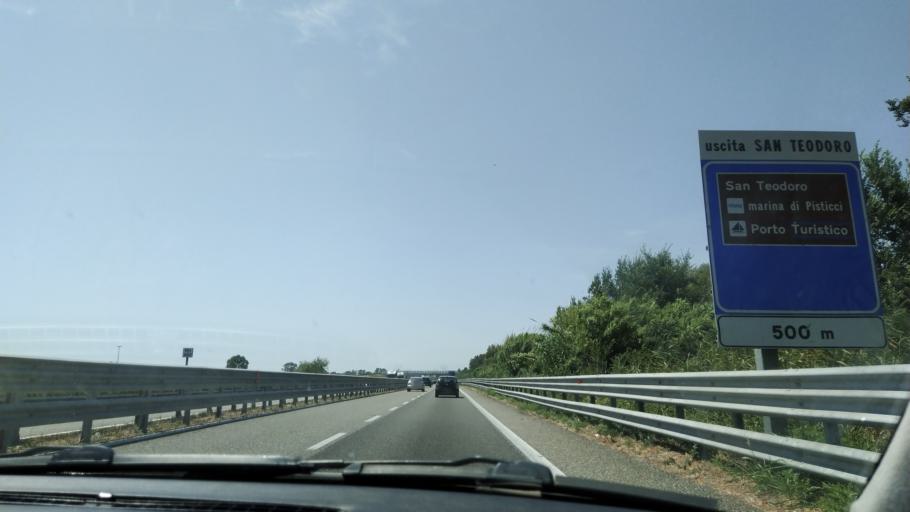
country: IT
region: Basilicate
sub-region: Provincia di Matera
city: Marconia
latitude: 40.3453
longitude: 16.7648
